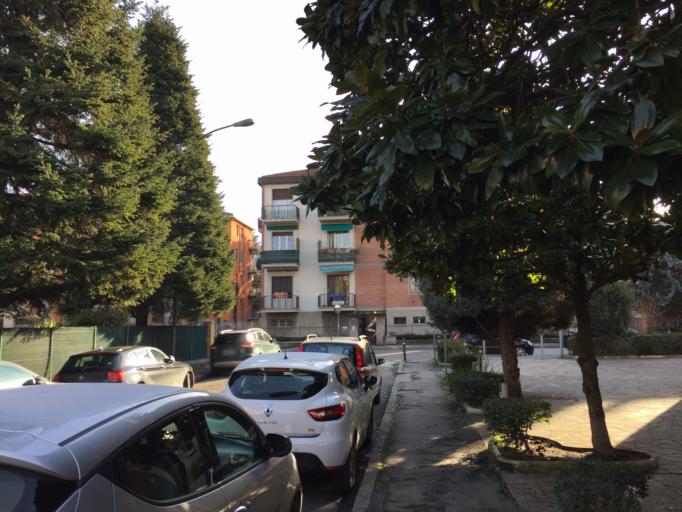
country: IT
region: Emilia-Romagna
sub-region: Provincia di Bologna
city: Casalecchio di Reno
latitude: 44.4964
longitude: 11.2943
